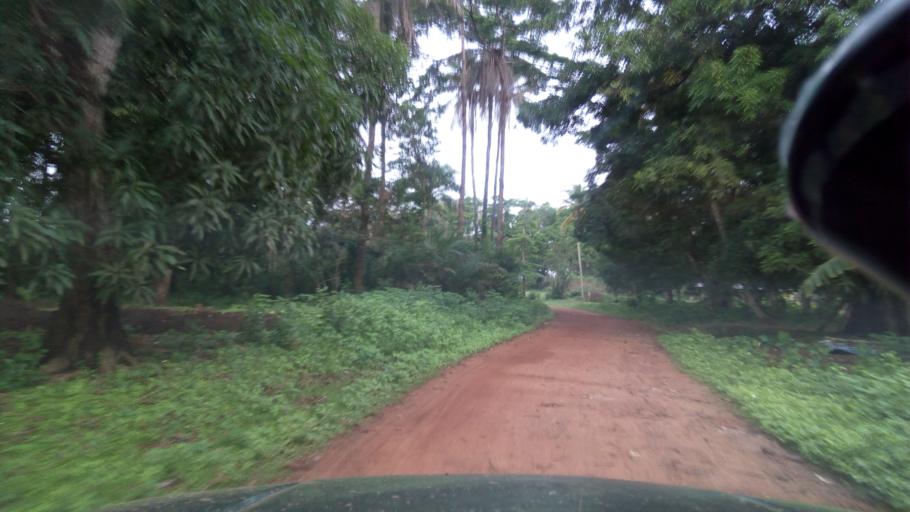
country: SL
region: Northern Province
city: Port Loko
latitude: 8.7220
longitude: -12.8004
